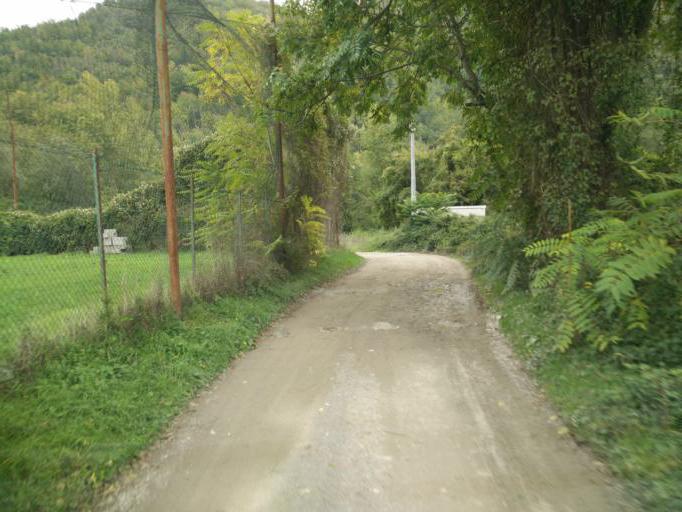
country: IT
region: Tuscany
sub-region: Provincia di Massa-Carrara
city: Casola in Lunigiana
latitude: 44.1984
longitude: 10.1731
